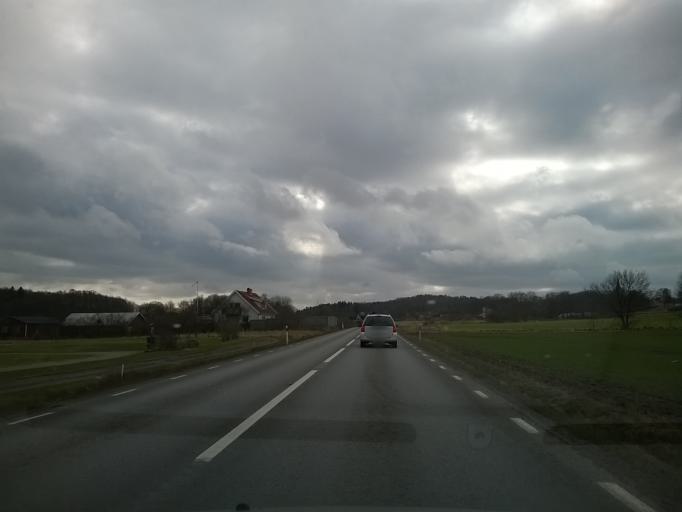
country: SE
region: Halland
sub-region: Varbergs Kommun
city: Tvaaker
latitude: 57.1364
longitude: 12.3953
